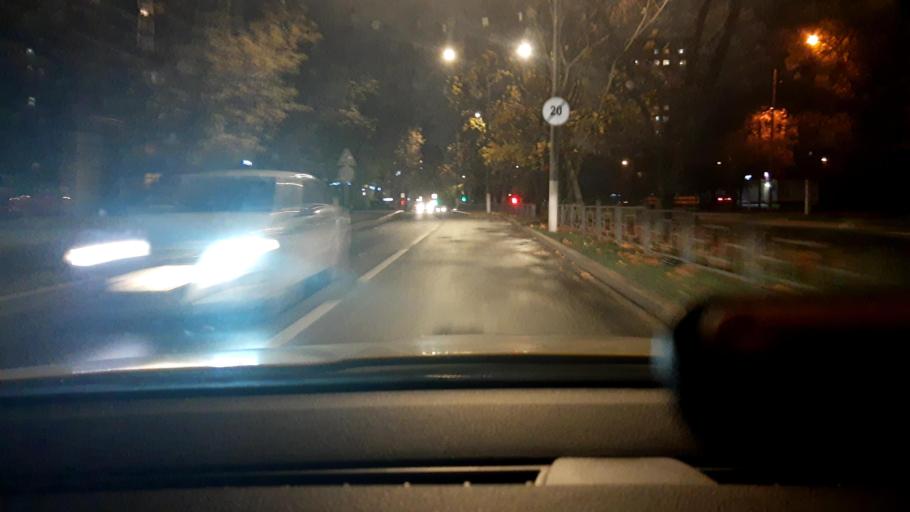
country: RU
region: Moscow
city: Tekstil'shchiki
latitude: 55.6979
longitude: 37.7384
